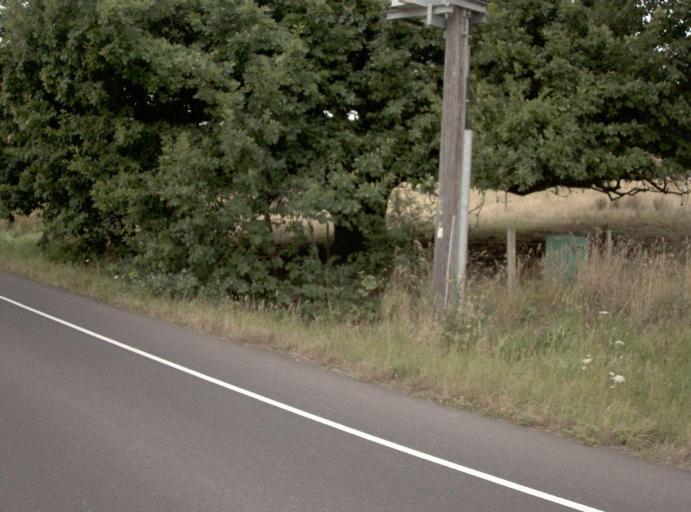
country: AU
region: Victoria
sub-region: Yarra Ranges
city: Yarra Glen
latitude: -37.6717
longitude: 145.3815
